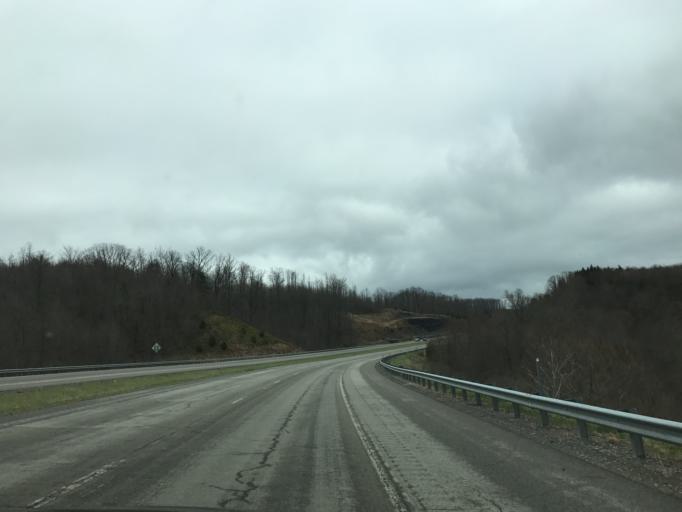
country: US
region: West Virginia
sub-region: Raleigh County
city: Sophia
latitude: 37.7178
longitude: -81.2784
